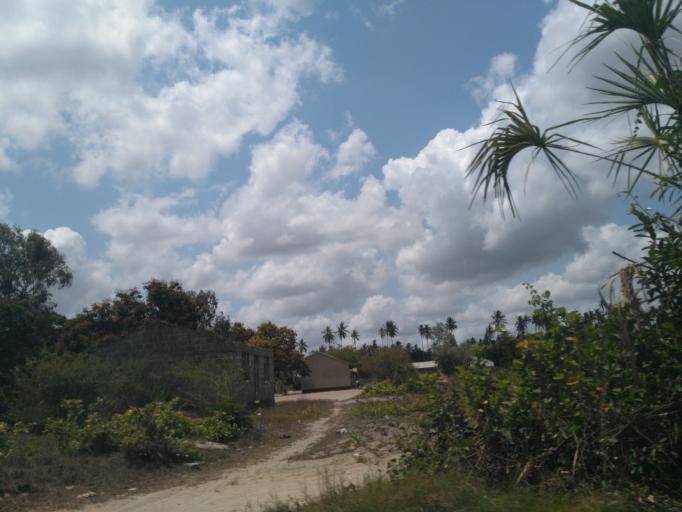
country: TZ
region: Dar es Salaam
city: Dar es Salaam
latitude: -6.8793
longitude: 39.3392
